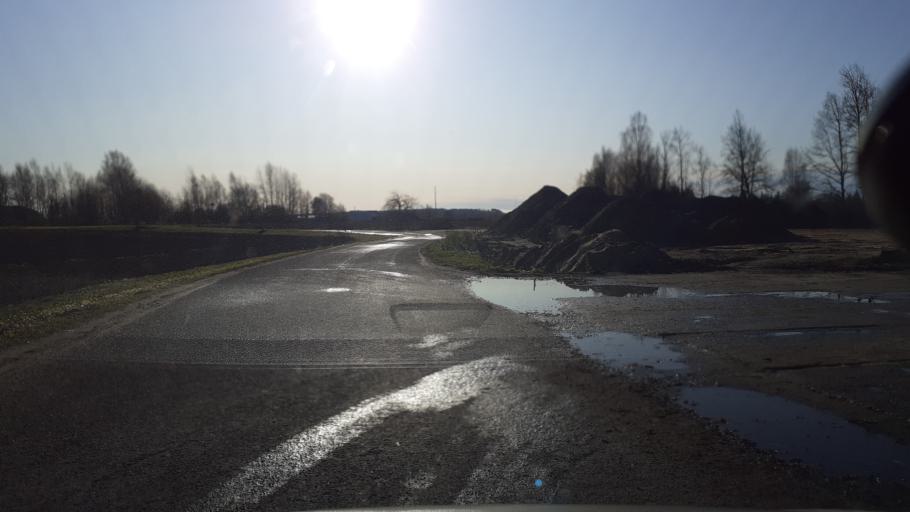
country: LV
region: Kuldigas Rajons
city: Kuldiga
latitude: 56.9987
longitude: 21.8905
